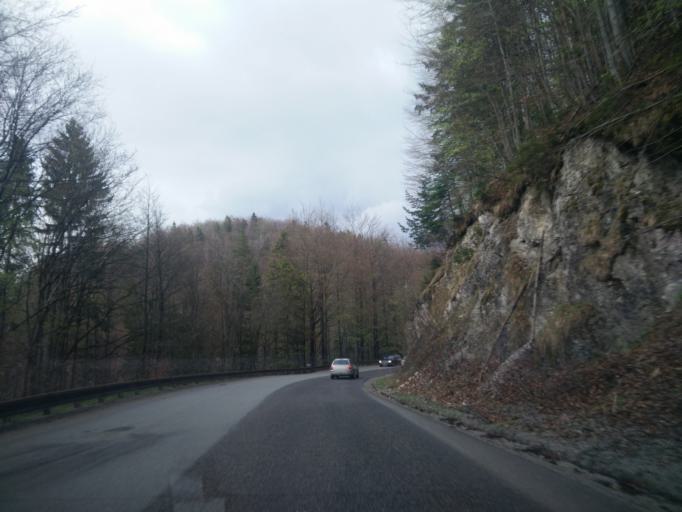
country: SK
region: Banskobystricky
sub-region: Okres Ziar nad Hronom
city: Kremnica
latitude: 48.8342
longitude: 18.9920
